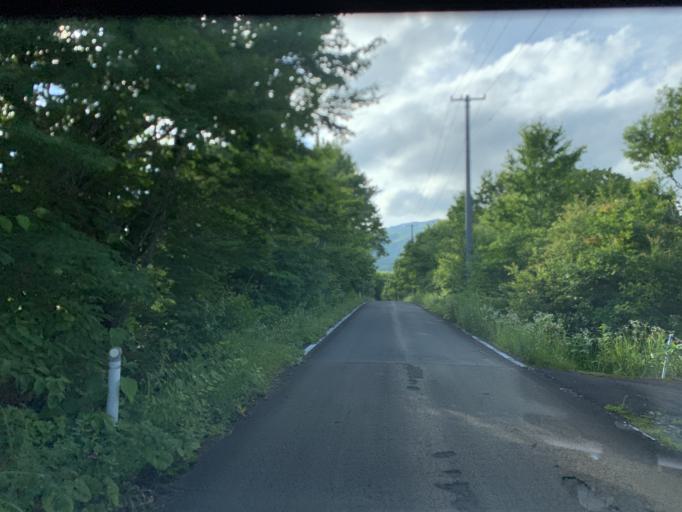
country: JP
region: Iwate
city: Ichinoseki
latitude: 38.9233
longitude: 140.8363
